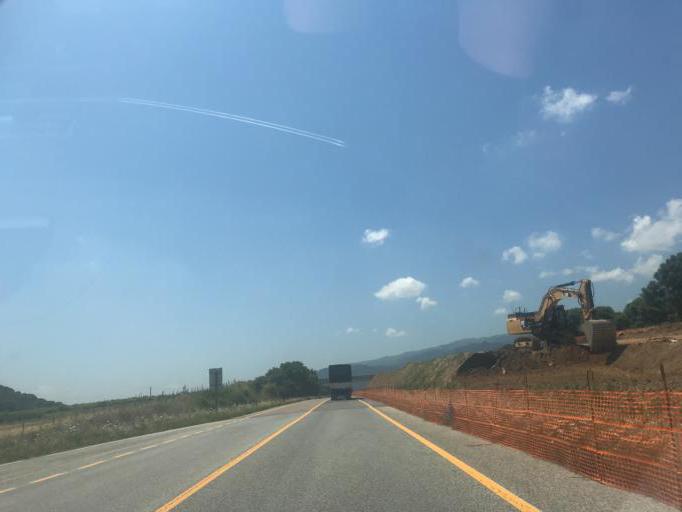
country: IT
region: Sardinia
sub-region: Provincia di Olbia-Tempio
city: Berchidda
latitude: 40.7795
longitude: 9.2303
